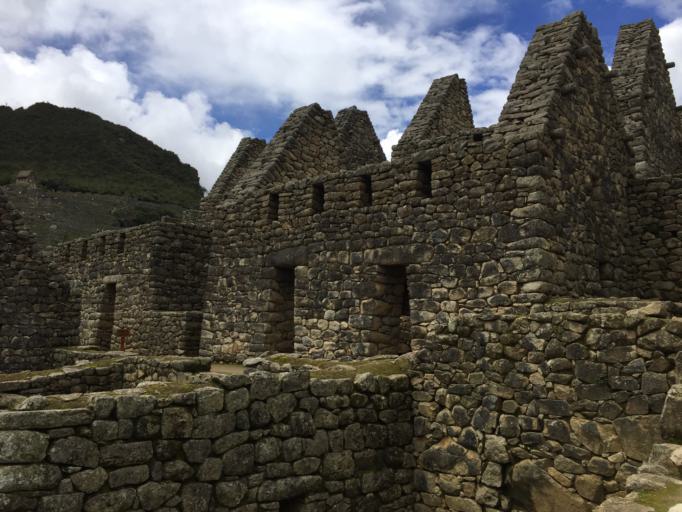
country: PE
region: Cusco
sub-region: Provincia de La Convencion
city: Santa Teresa
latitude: -13.1625
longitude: -72.5447
